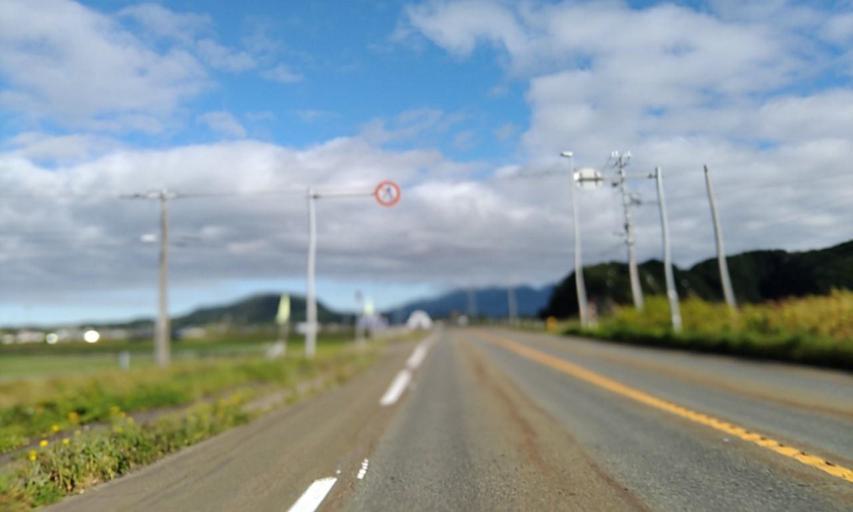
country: JP
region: Hokkaido
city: Shizunai-furukawacho
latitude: 42.2168
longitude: 142.6416
